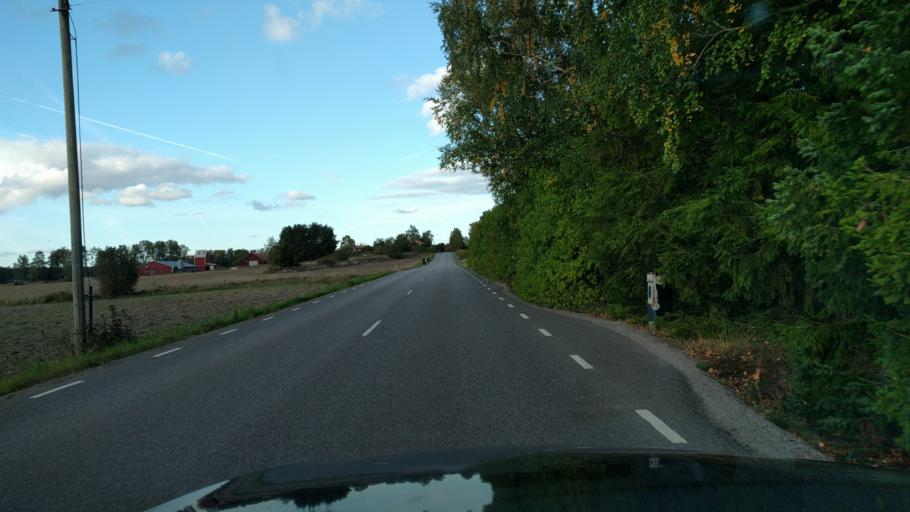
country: SE
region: Uppsala
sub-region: Osthammars Kommun
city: Bjorklinge
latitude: 60.1498
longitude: 17.5843
